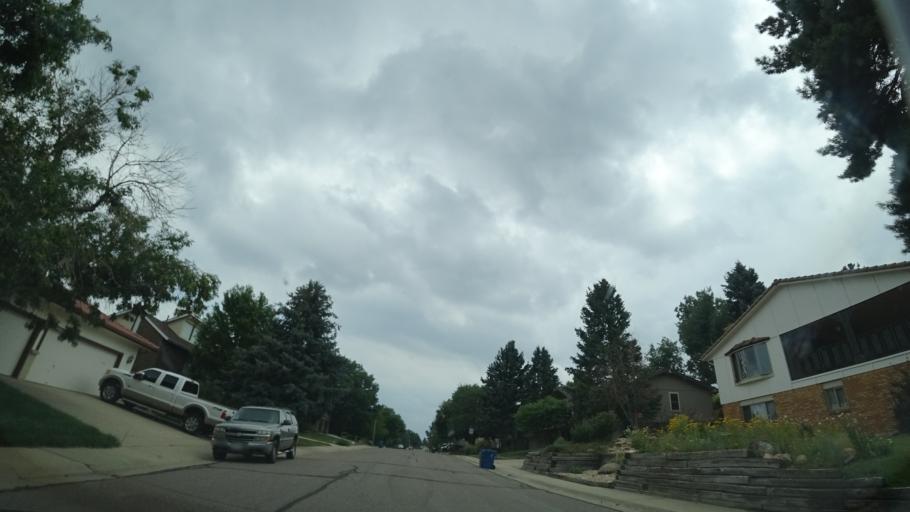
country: US
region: Colorado
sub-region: Jefferson County
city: West Pleasant View
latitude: 39.7083
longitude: -105.1621
